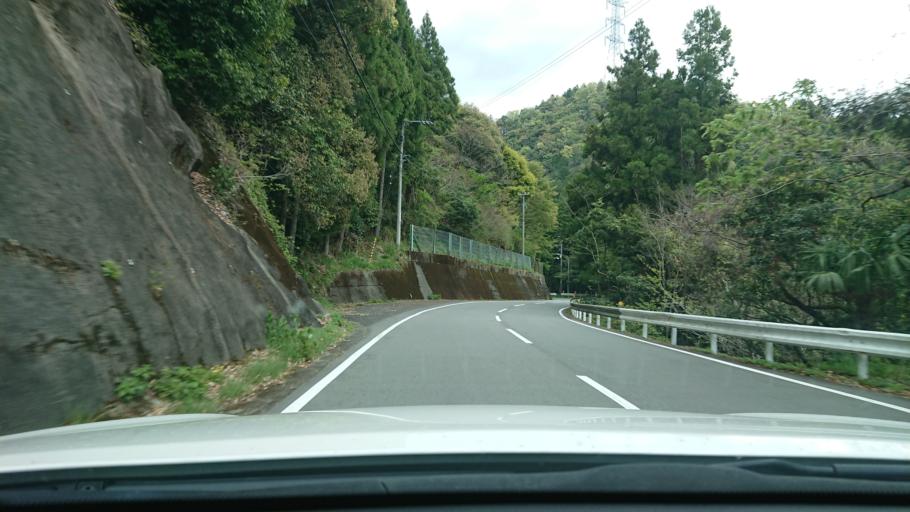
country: JP
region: Tokushima
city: Ishii
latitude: 33.9093
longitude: 134.4206
